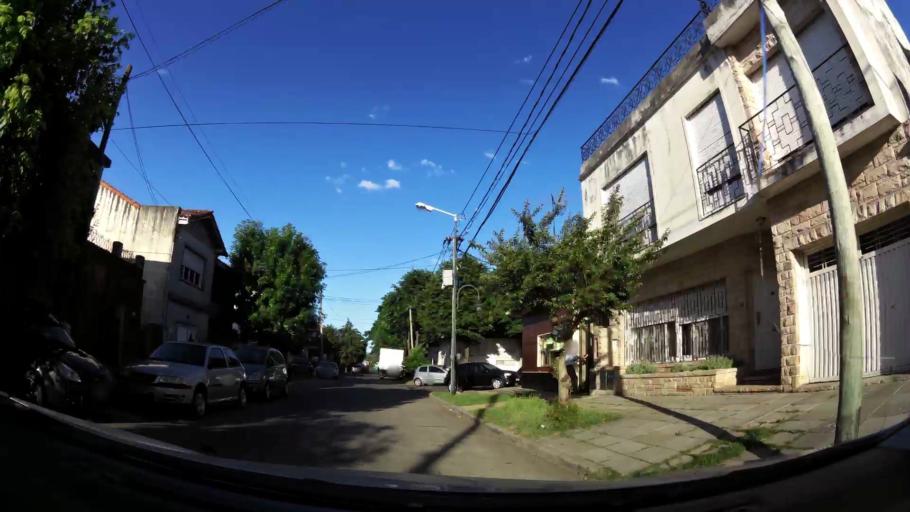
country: AR
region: Buenos Aires
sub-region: Partido de Tigre
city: Tigre
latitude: -34.4619
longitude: -58.5655
